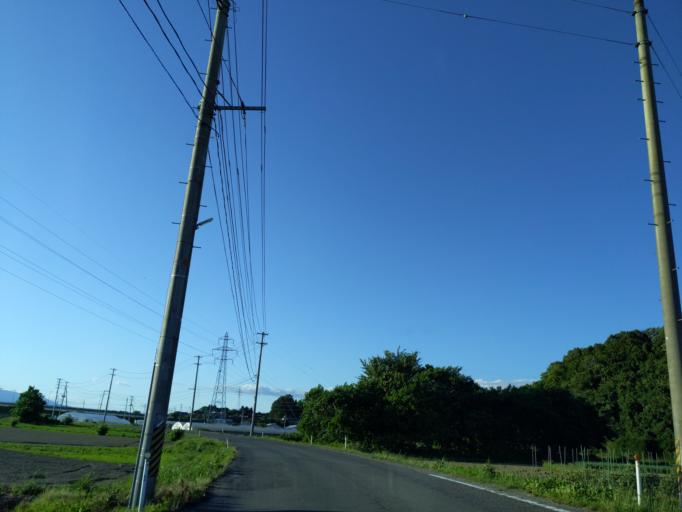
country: JP
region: Fukushima
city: Koriyama
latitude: 37.3904
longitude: 140.4122
